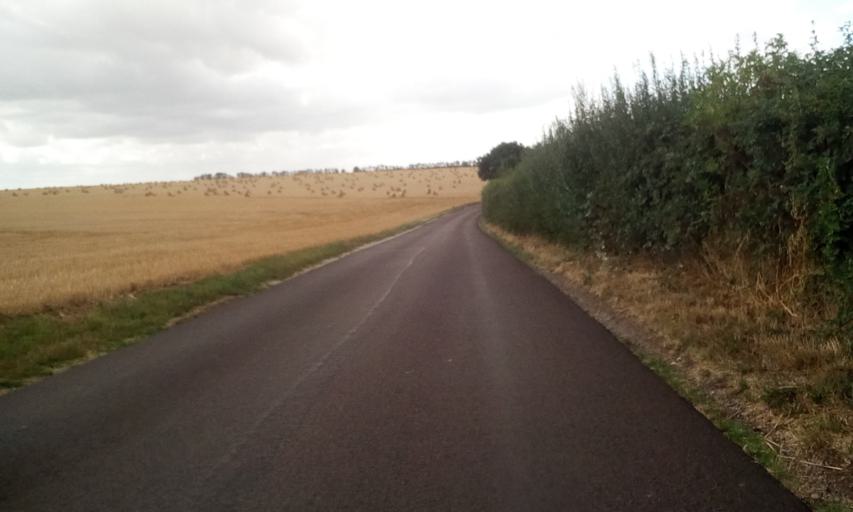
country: FR
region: Lower Normandy
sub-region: Departement du Calvados
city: Courseulles-sur-Mer
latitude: 49.2971
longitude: -0.4761
